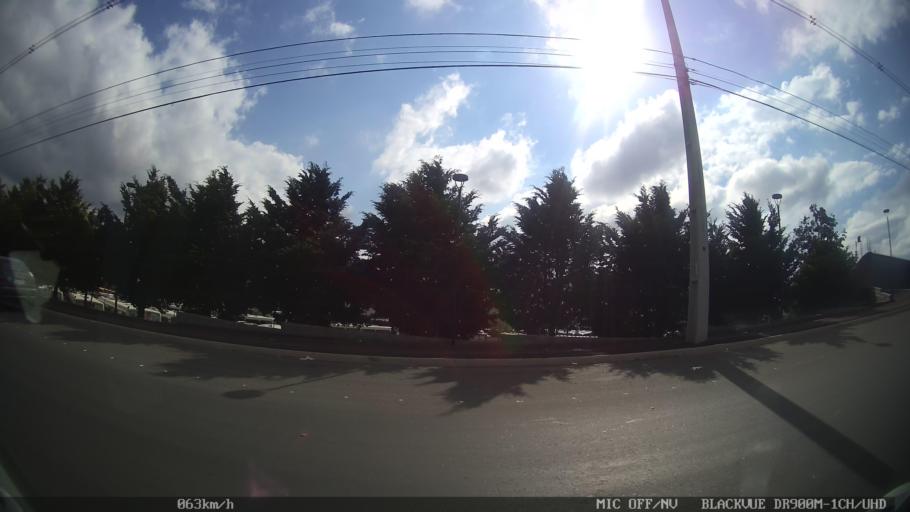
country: BR
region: Parana
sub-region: Pinhais
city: Pinhais
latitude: -25.3813
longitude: -49.1849
